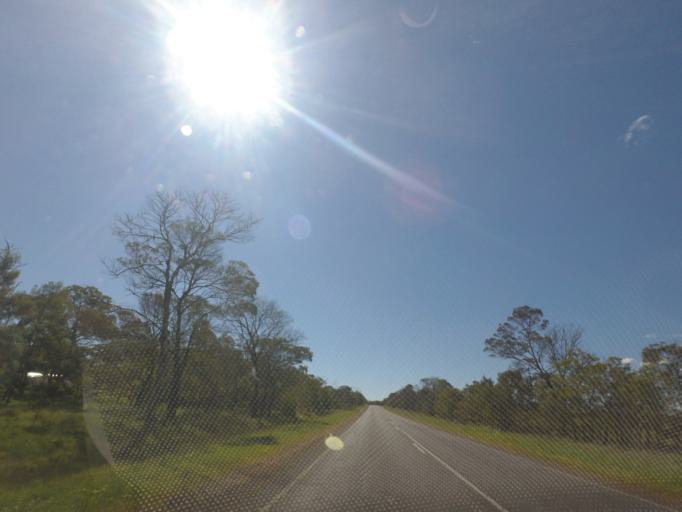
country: AU
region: Victoria
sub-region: Moorabool
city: Bacchus Marsh
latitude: -37.6384
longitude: 144.2200
